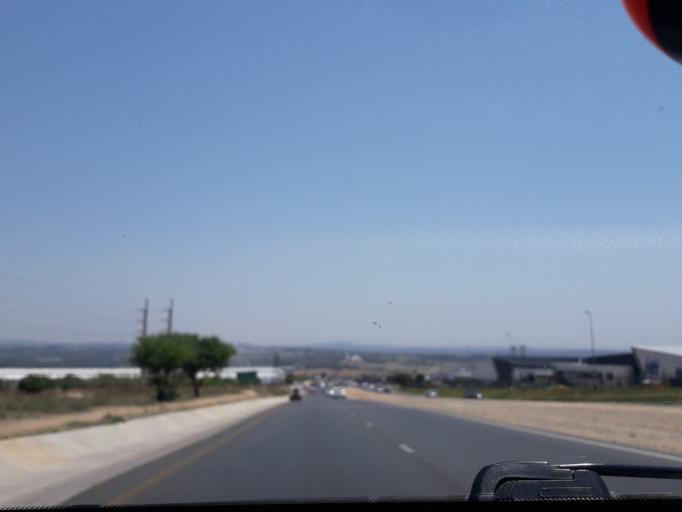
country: ZA
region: Gauteng
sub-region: City of Johannesburg Metropolitan Municipality
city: Midrand
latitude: -26.0162
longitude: 28.1259
